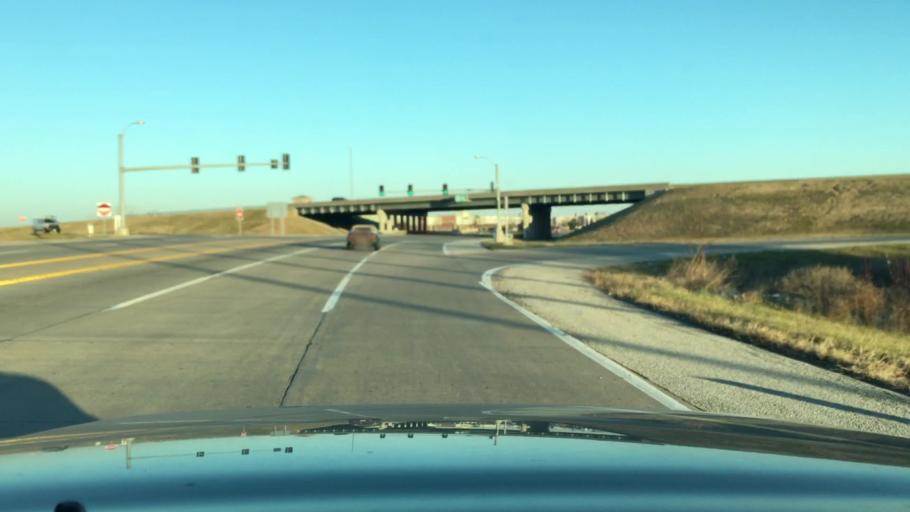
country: US
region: Missouri
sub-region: Saint Charles County
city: Saint Charles
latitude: 38.8228
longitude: -90.5174
